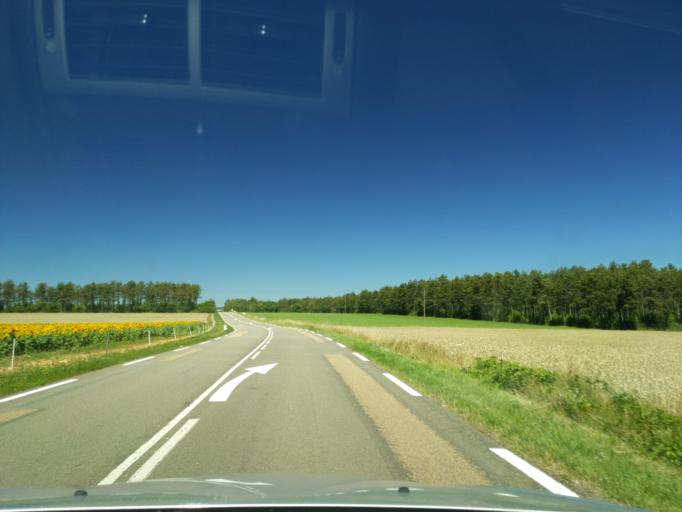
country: FR
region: Bourgogne
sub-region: Departement de la Cote-d'Or
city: Is-sur-Tille
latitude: 47.5012
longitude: 5.0836
